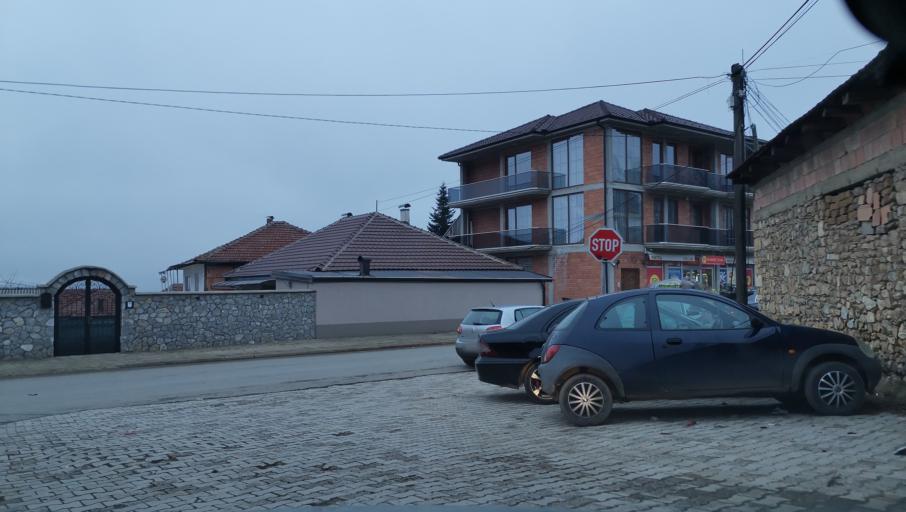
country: MK
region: Debar
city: Debar
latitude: 41.5284
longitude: 20.5230
